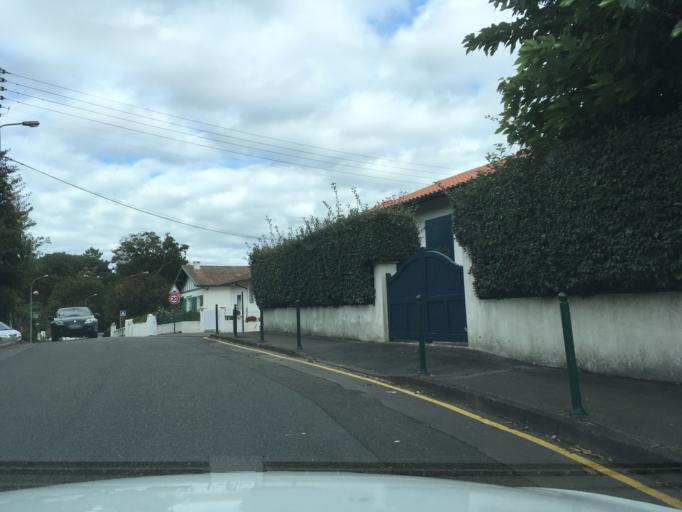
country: FR
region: Aquitaine
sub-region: Departement des Pyrenees-Atlantiques
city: Biarritz
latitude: 43.4625
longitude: -1.5508
